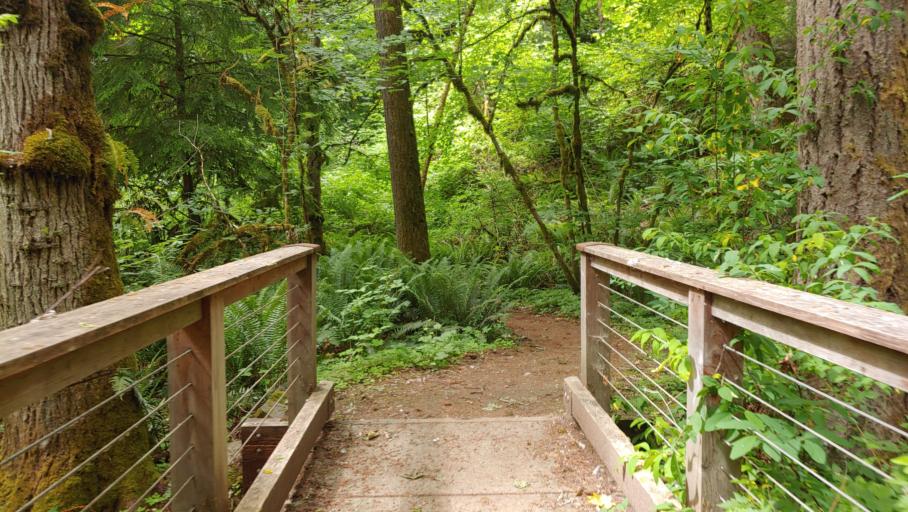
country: US
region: Washington
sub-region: King County
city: Newcastle
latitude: 47.5192
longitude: -122.1622
